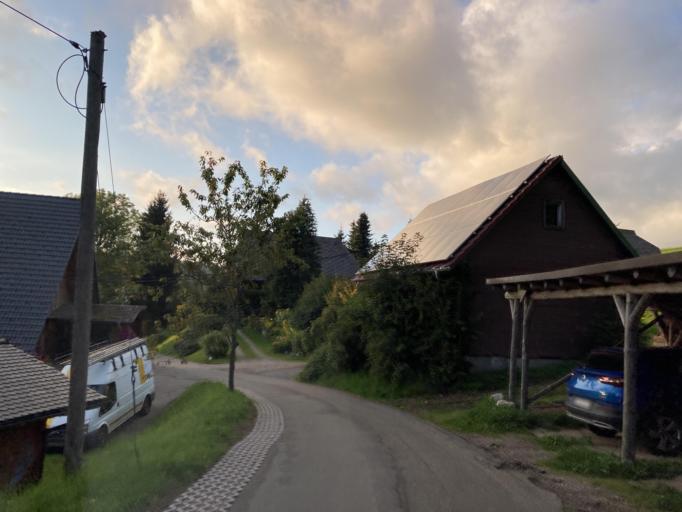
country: DE
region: Baden-Wuerttemberg
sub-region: Freiburg Region
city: Vohrenbach
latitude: 48.0795
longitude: 8.2781
